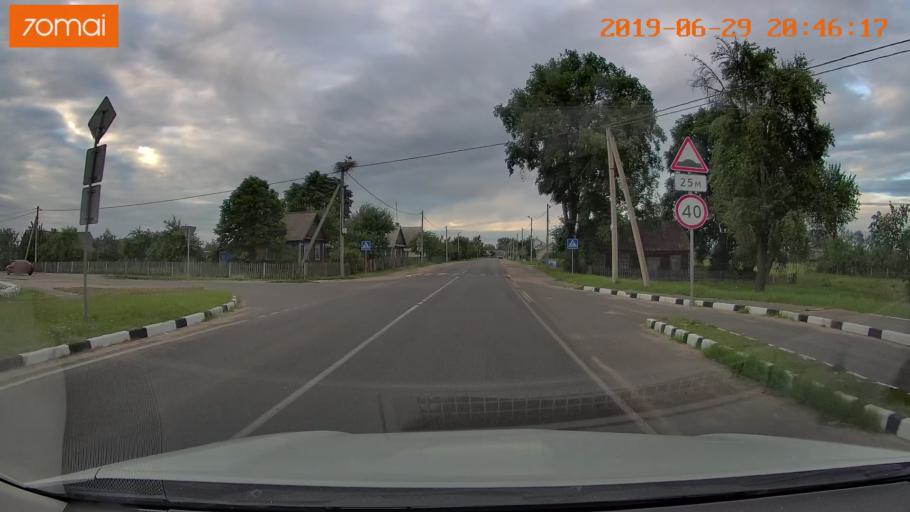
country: BY
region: Brest
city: Hantsavichy
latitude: 52.6299
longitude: 26.3078
